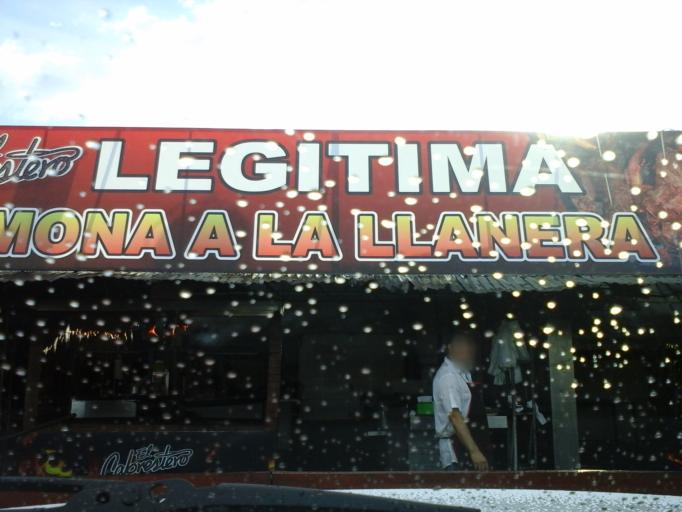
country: CO
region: Meta
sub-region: Villavicencio
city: Villavicencio
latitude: 4.1203
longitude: -73.6162
